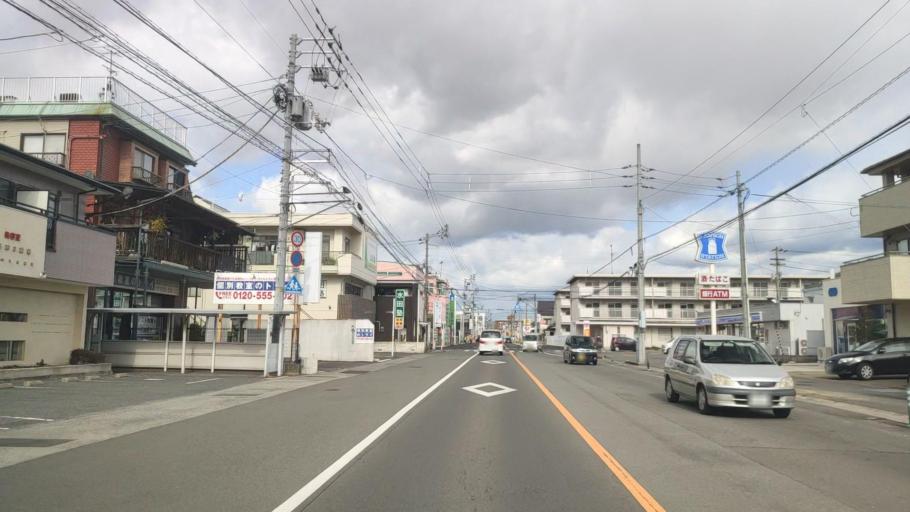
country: JP
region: Ehime
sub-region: Shikoku-chuo Shi
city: Matsuyama
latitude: 33.8120
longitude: 132.7608
